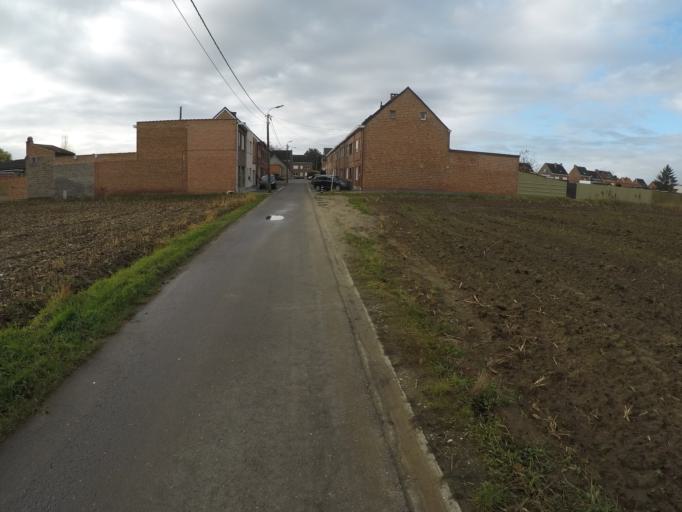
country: BE
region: Flanders
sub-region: Provincie Vlaams-Brabant
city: Londerzeel
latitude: 51.0156
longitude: 4.2966
